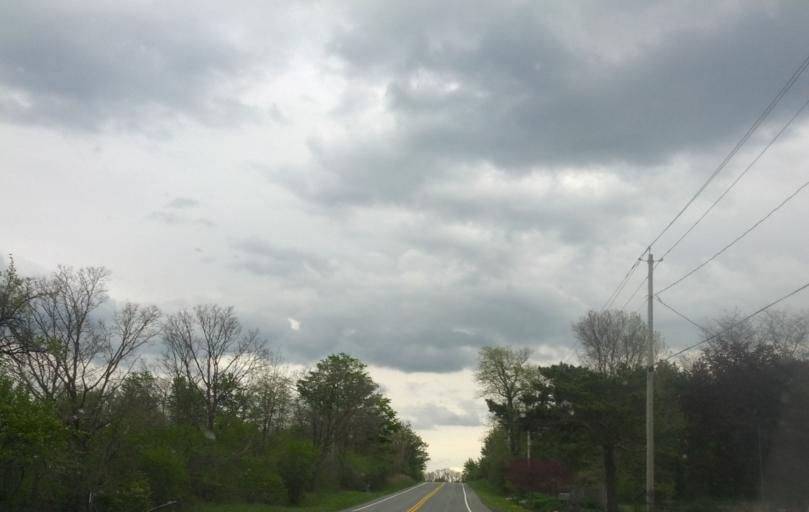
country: US
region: New York
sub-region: Onondaga County
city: Fayetteville
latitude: 42.9929
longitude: -76.0399
